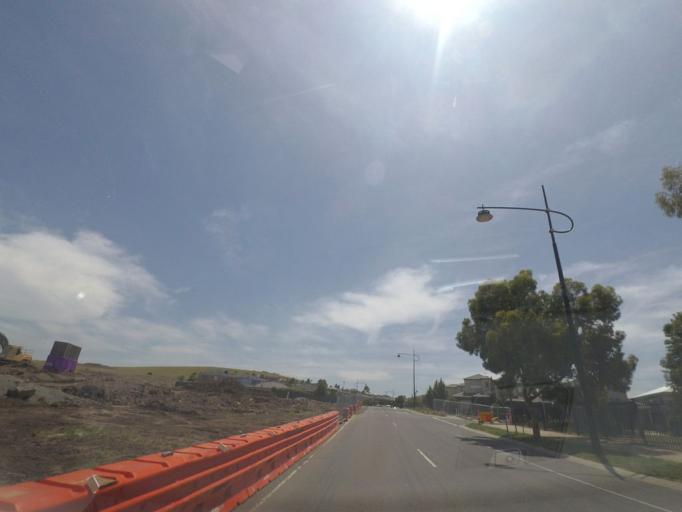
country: AU
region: Victoria
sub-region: Hume
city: Roxburgh Park
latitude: -37.6143
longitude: 144.9085
